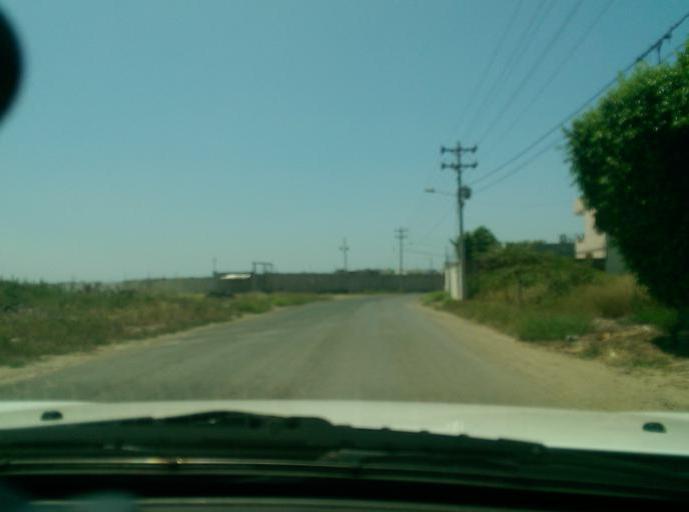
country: EC
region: Manabi
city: Manta
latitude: -0.9628
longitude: -80.7595
